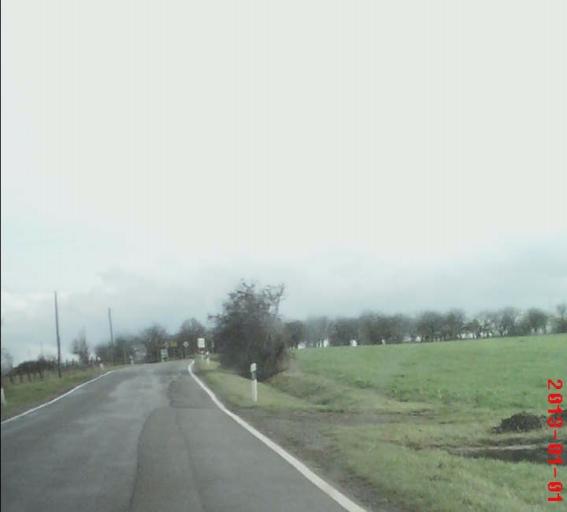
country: DE
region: Thuringia
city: Muehlhausen
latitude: 51.2295
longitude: 10.4156
